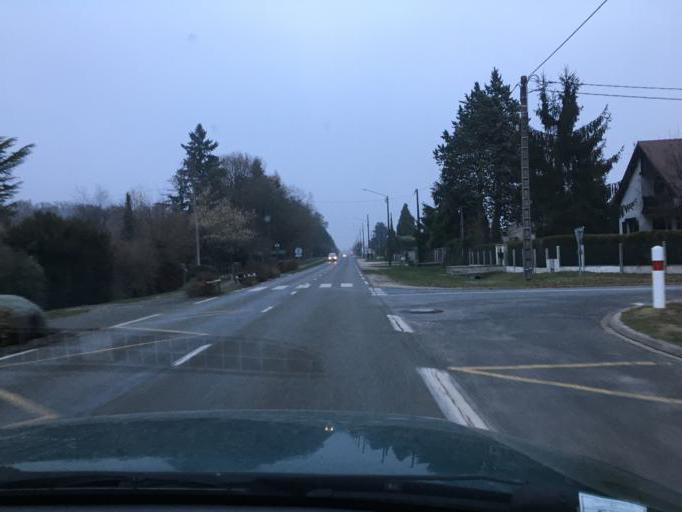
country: FR
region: Centre
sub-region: Departement du Loiret
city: Lailly-en-Val
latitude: 47.7632
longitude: 1.6817
